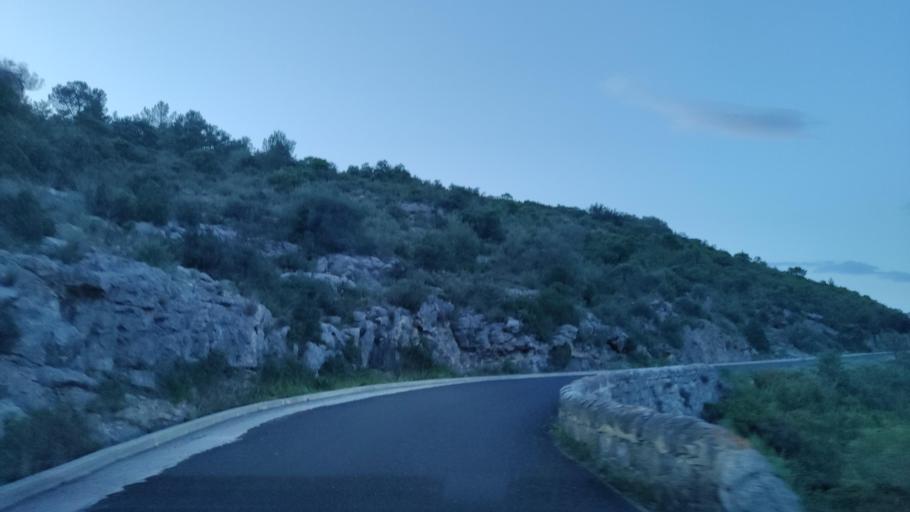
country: FR
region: Languedoc-Roussillon
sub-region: Departement des Pyrenees-Orientales
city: Estagel
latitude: 42.8550
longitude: 2.7686
